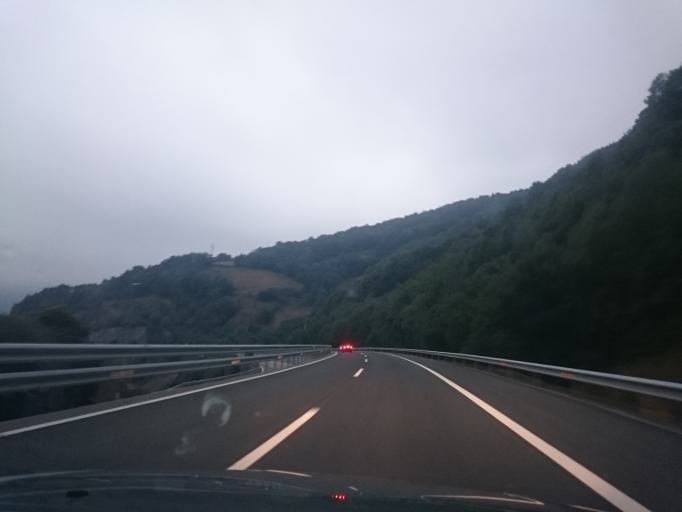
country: ES
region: Asturias
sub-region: Province of Asturias
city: Pola de Lena
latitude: 43.0527
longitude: -5.8202
